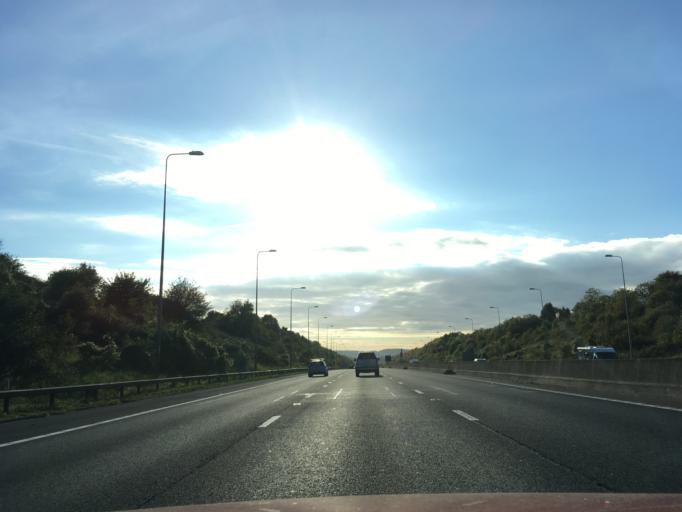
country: GB
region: England
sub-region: South Gloucestershire
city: Severn Beach
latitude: 51.5214
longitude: -2.6306
